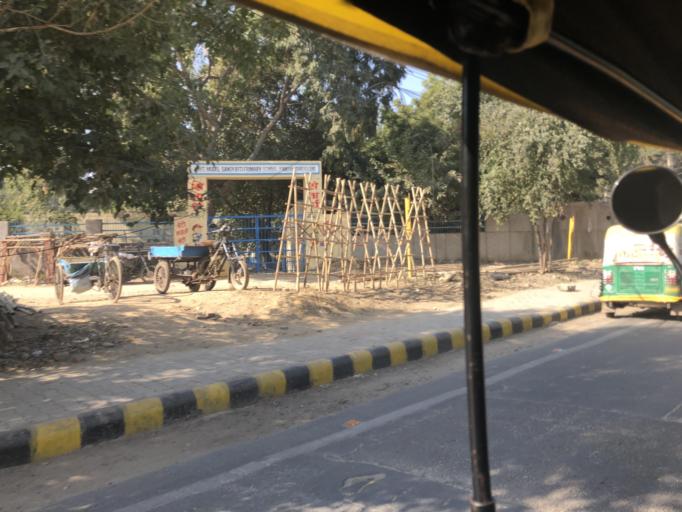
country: IN
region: Haryana
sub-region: Gurgaon
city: Gurgaon
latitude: 28.4469
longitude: 77.0753
